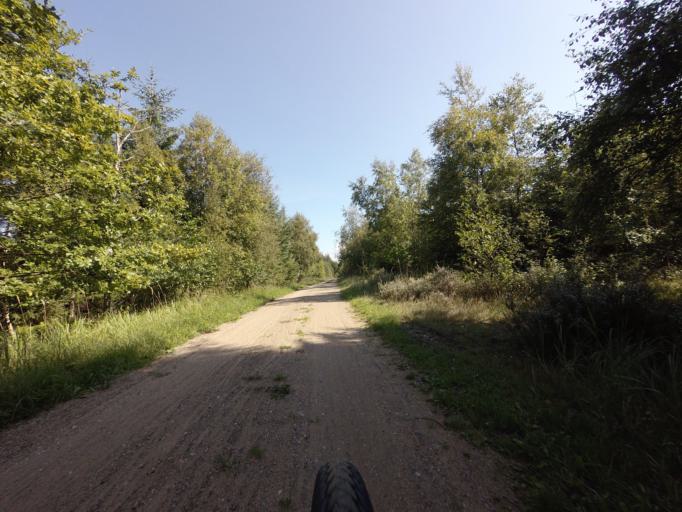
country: DK
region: North Denmark
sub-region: Hjorring Kommune
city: Hirtshals
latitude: 57.5847
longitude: 10.0977
